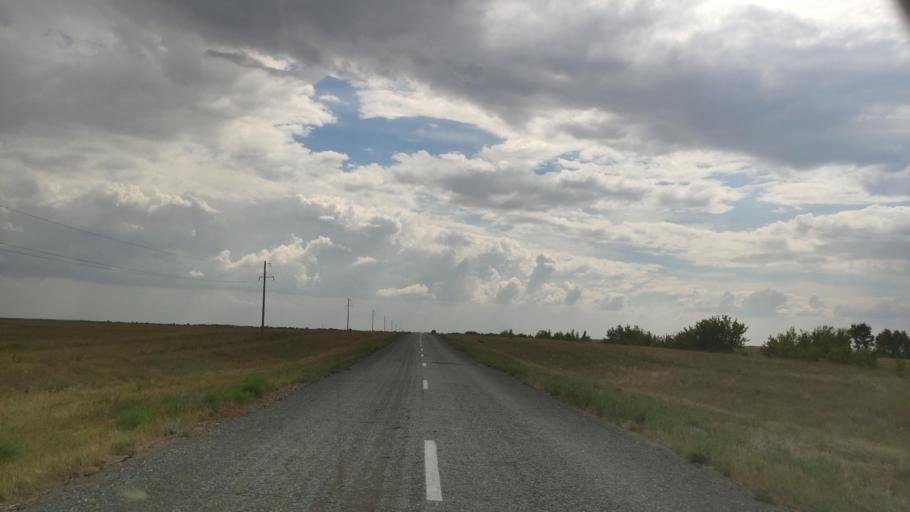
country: KZ
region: Pavlodar
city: Pavlodar
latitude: 52.5648
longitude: 77.3374
